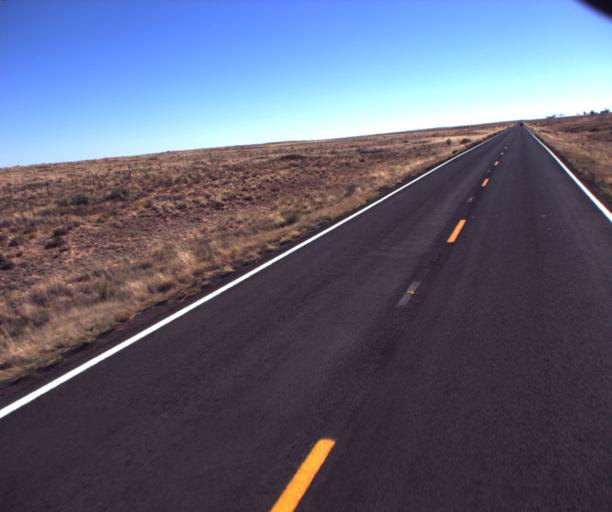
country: US
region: Arizona
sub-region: Coconino County
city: Tuba City
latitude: 35.9655
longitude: -110.9506
